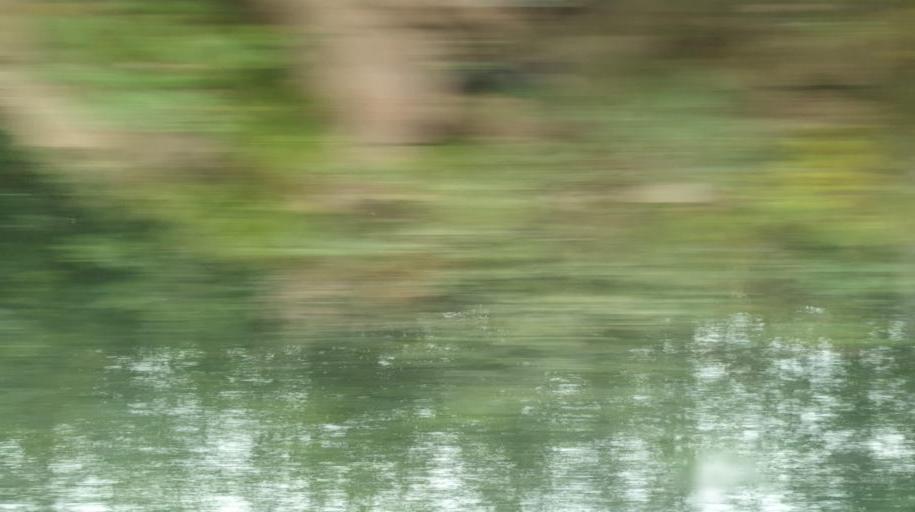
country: NO
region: Buskerud
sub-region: Drammen
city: Skoger
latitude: 59.6931
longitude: 10.2426
